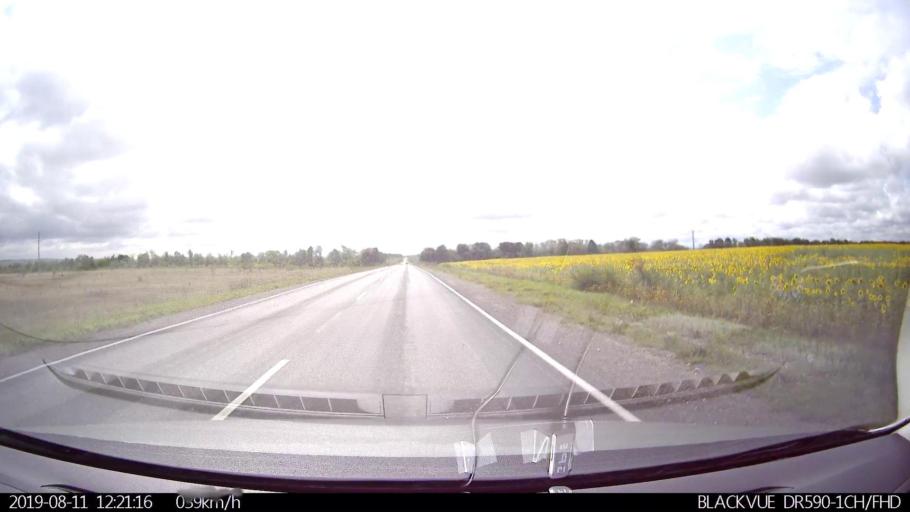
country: RU
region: Ulyanovsk
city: Ignatovka
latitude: 53.9225
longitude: 47.9580
